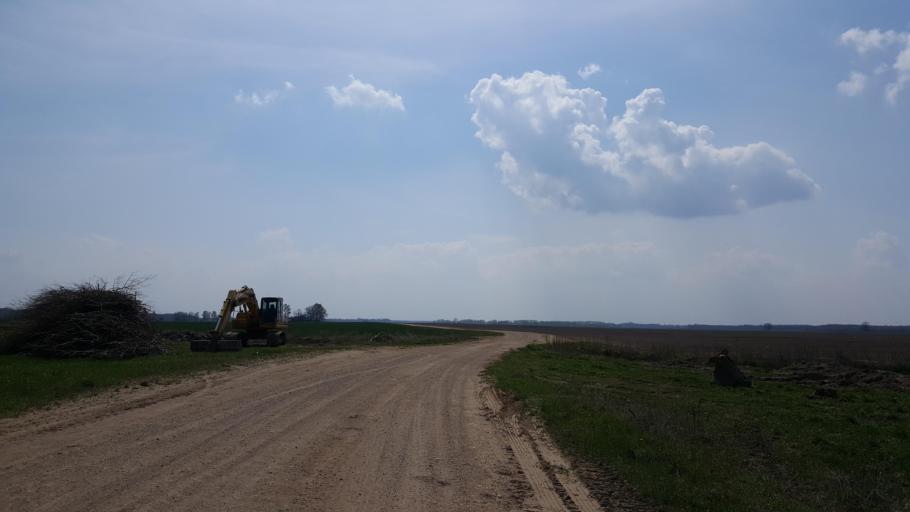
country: BY
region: Brest
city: Kamyanyets
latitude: 52.3033
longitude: 23.9058
